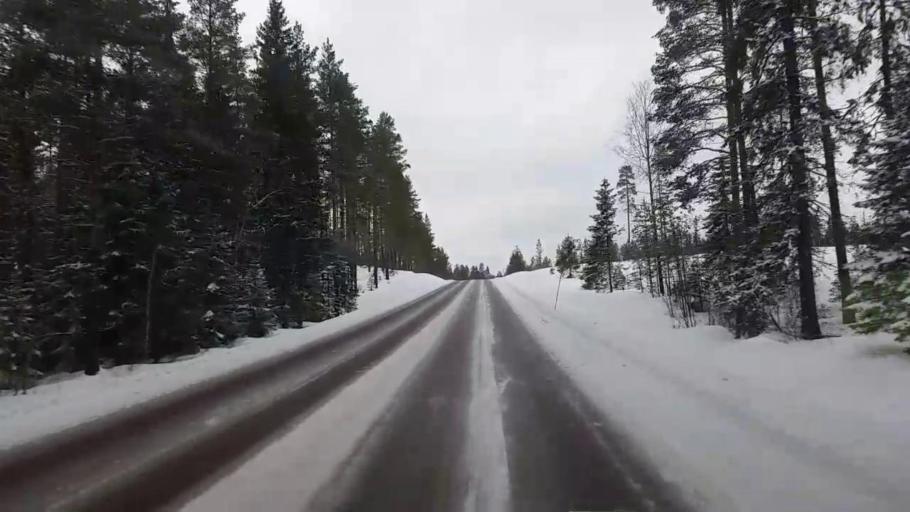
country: SE
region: Jaemtland
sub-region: Bergs Kommun
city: Hoverberg
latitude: 62.4249
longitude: 14.6021
